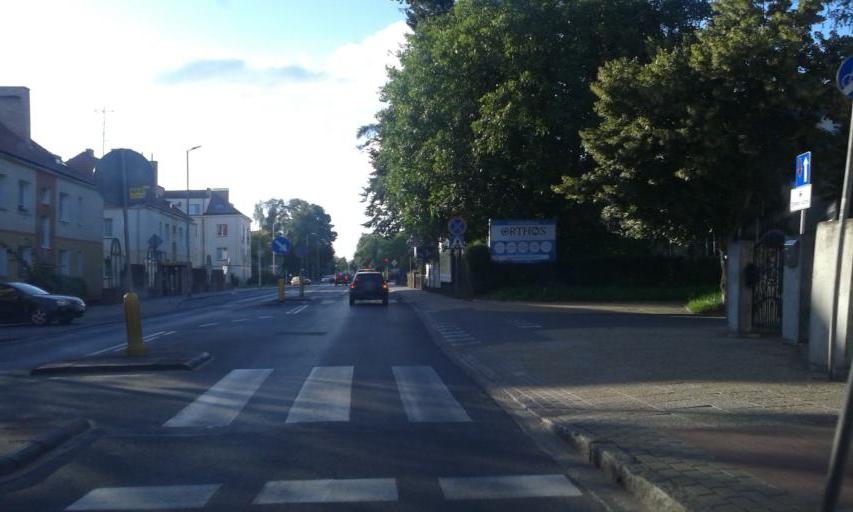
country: PL
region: West Pomeranian Voivodeship
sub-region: Koszalin
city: Koszalin
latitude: 54.1954
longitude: 16.2068
